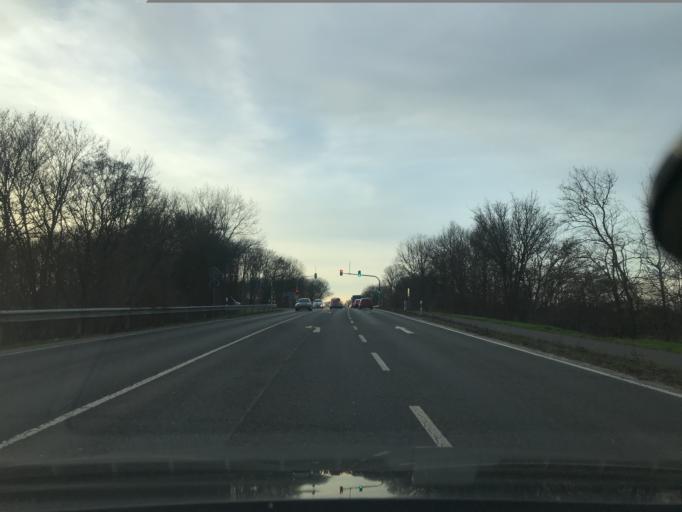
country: DE
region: North Rhine-Westphalia
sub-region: Regierungsbezirk Dusseldorf
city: Willich
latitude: 51.2526
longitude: 6.4963
